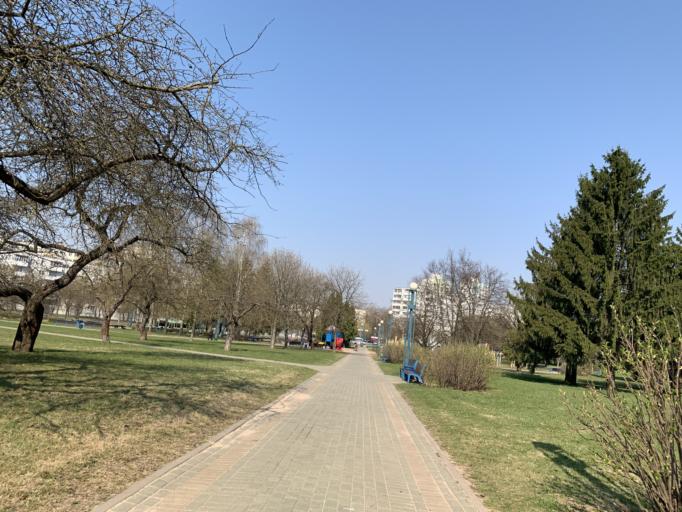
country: BY
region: Minsk
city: Borovlyany
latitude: 53.9379
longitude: 27.6565
